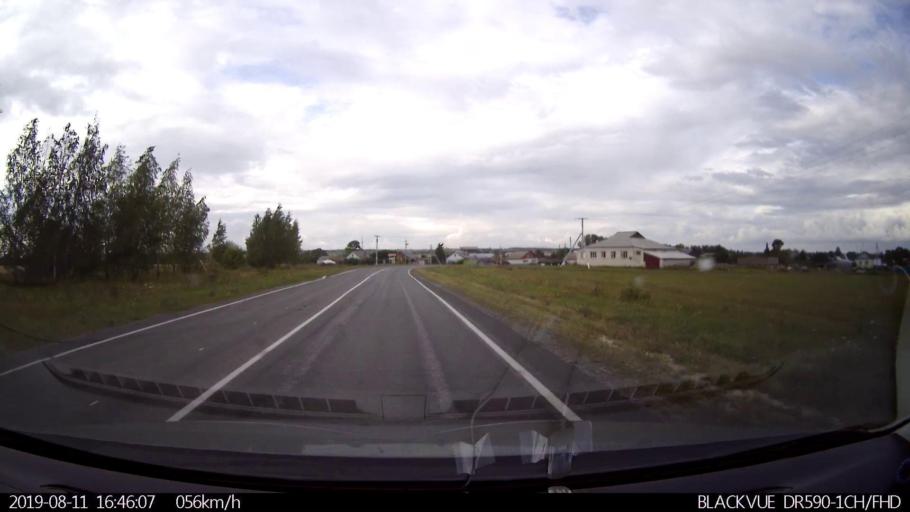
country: RU
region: Ulyanovsk
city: Mayna
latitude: 54.1959
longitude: 47.6889
